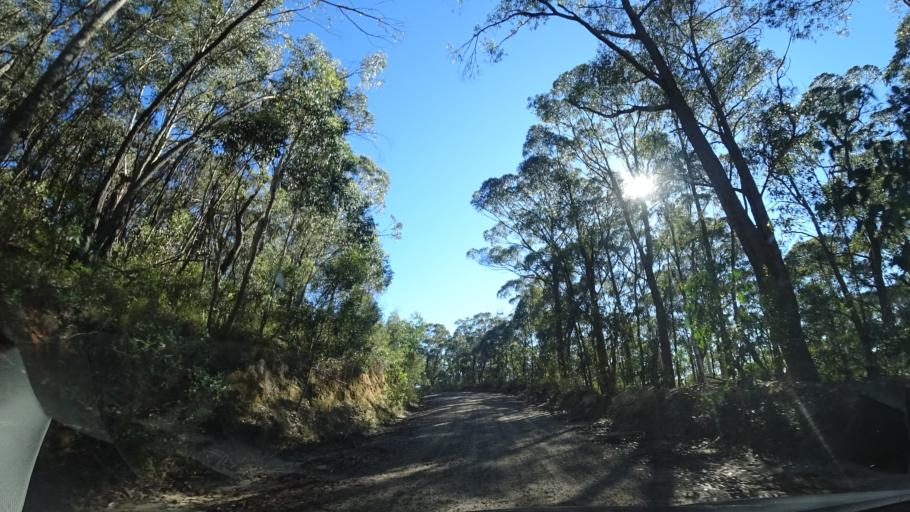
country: AU
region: New South Wales
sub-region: Lithgow
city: Lithgow
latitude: -33.4910
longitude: 150.2675
